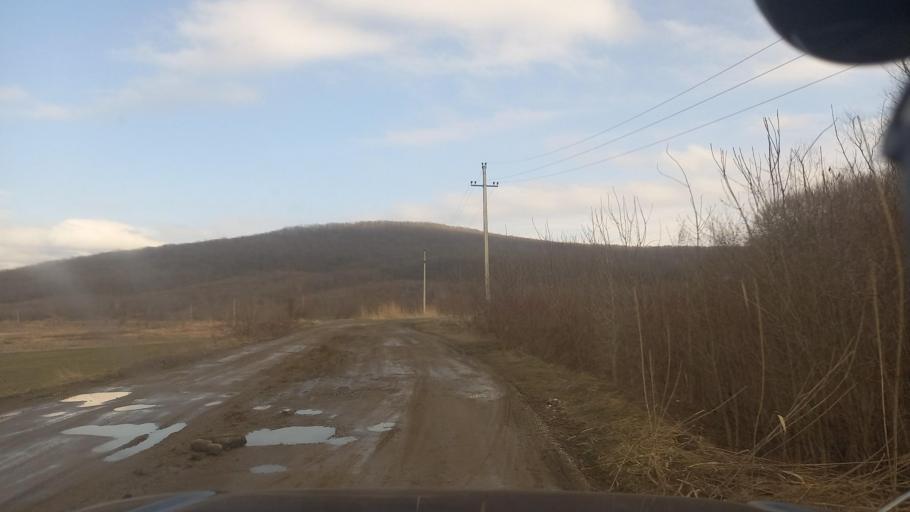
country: RU
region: Krasnodarskiy
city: Smolenskaya
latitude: 44.7560
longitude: 38.7842
